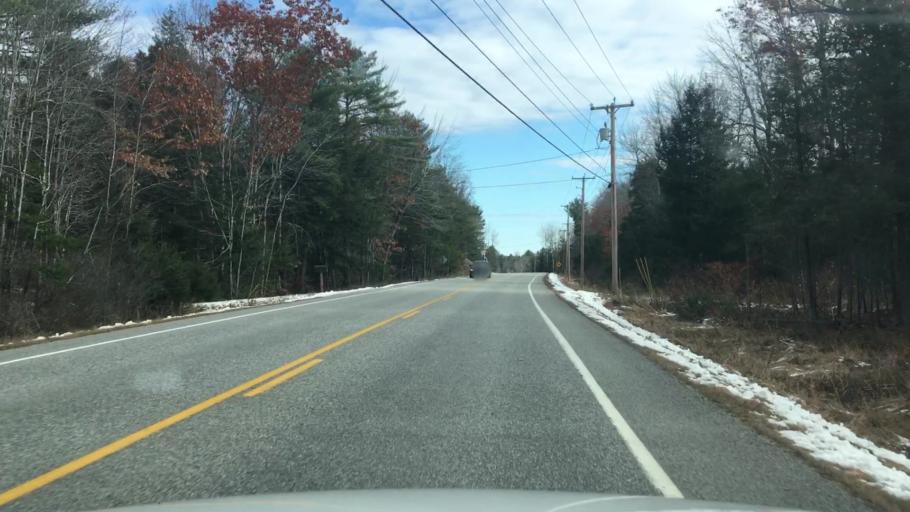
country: US
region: Maine
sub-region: Androscoggin County
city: Leeds
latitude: 44.3440
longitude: -70.1692
